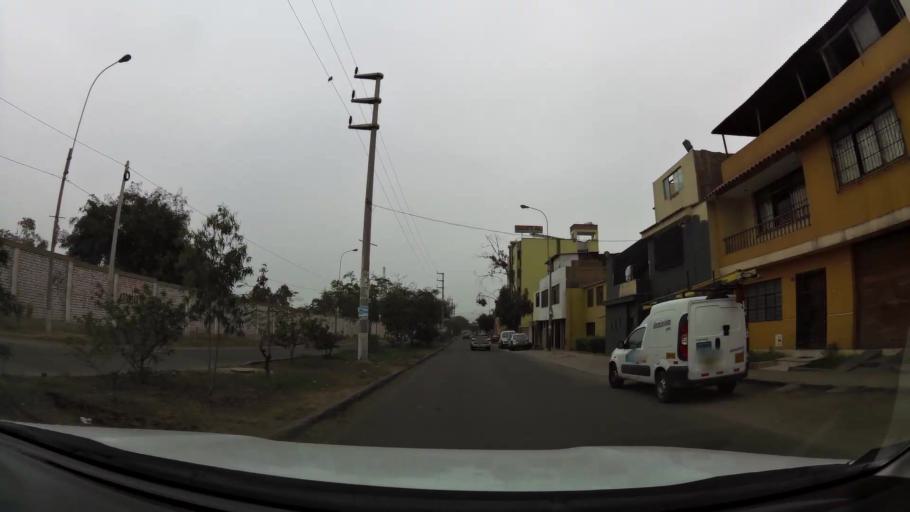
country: PE
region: Lima
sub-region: Lima
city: Surco
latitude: -12.1706
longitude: -76.9723
